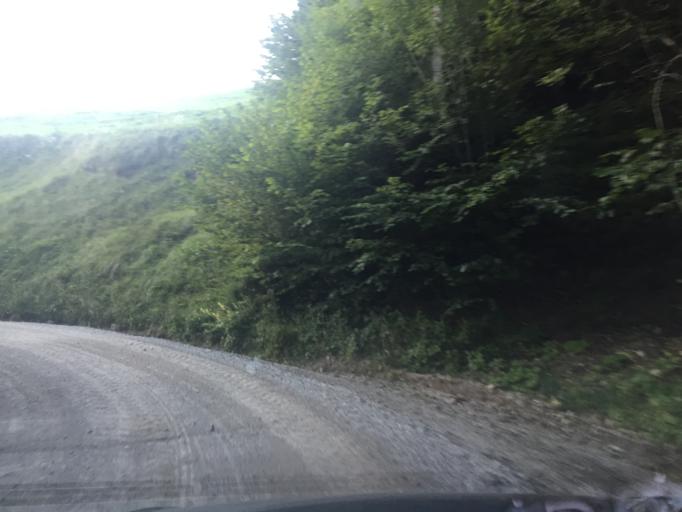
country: SI
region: Ravne na Koroskem
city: Kotlje
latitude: 46.4569
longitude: 14.9818
